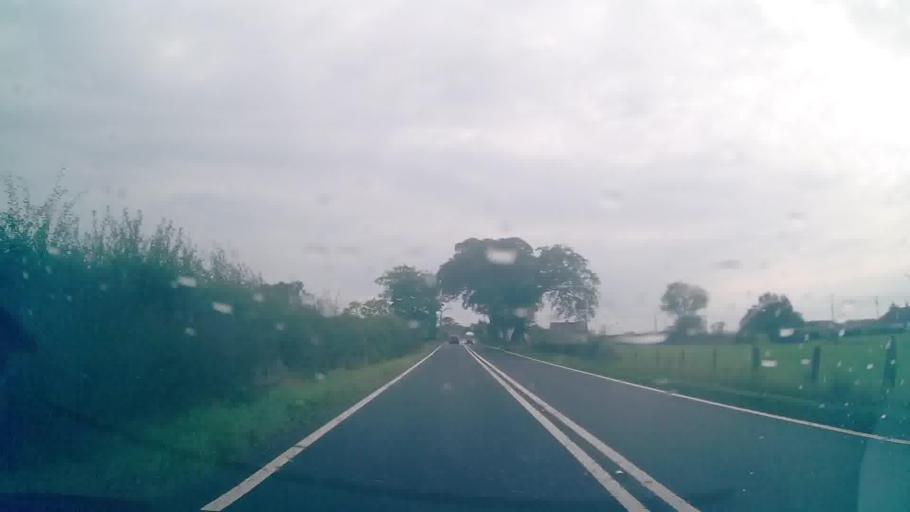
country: GB
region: Scotland
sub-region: Dumfries and Galloway
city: Lochmaben
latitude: 55.0628
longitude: -3.4945
